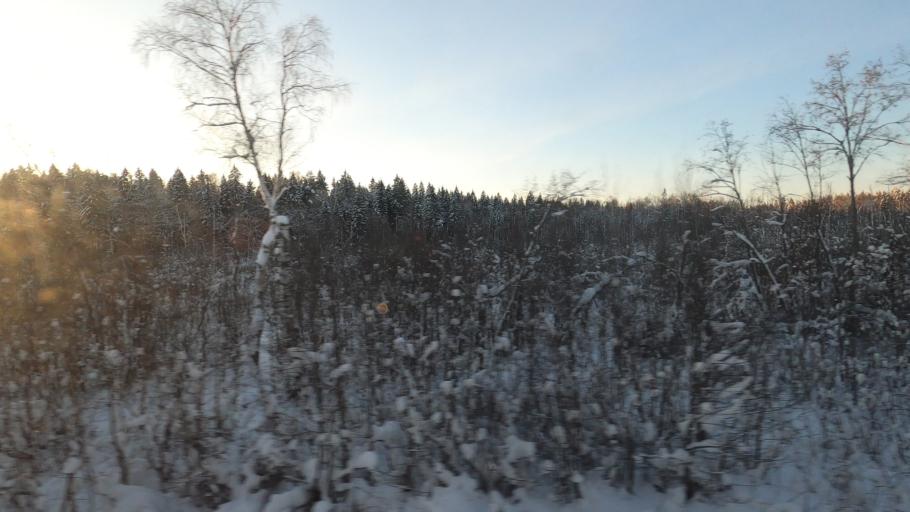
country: RU
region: Moskovskaya
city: Novo-Nikol'skoye
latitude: 56.5619
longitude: 37.5658
